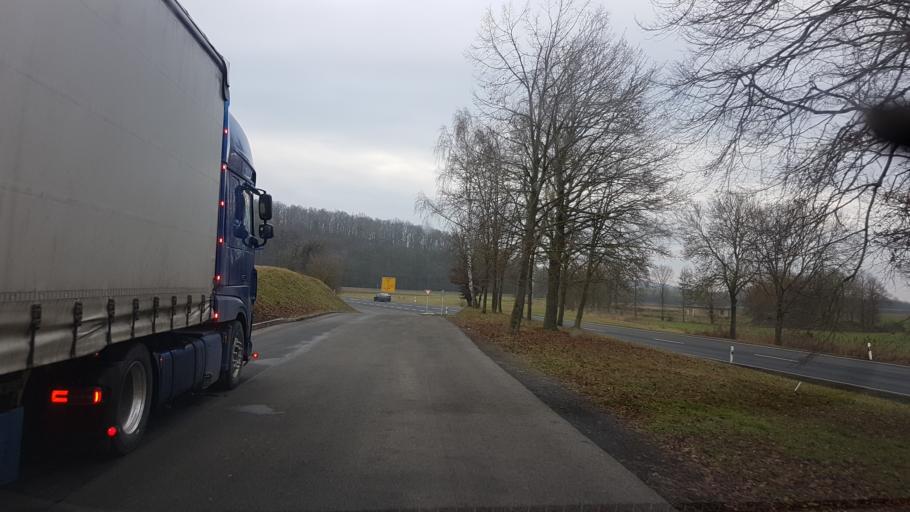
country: DE
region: Bavaria
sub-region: Regierungsbezirk Unterfranken
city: Ermershausen
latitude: 50.2317
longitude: 10.5692
